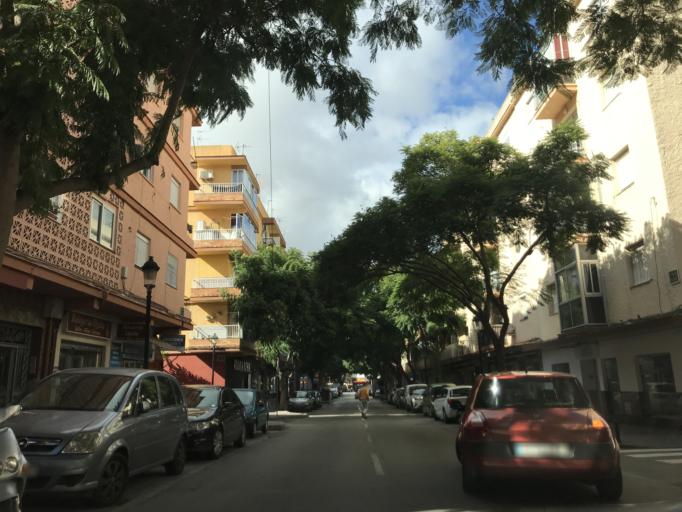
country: ES
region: Andalusia
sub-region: Provincia de Malaga
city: Fuengirola
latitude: 36.5395
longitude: -4.6288
